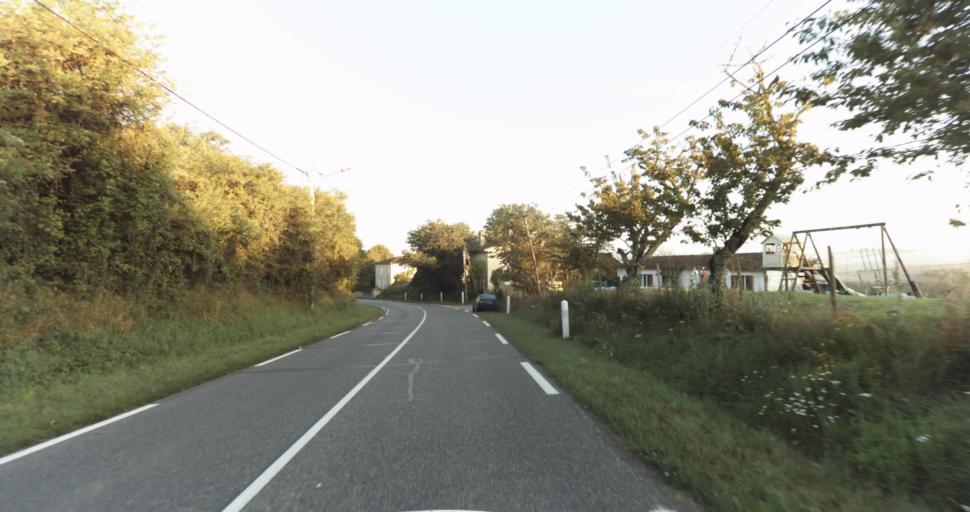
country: FR
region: Aquitaine
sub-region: Departement de la Gironde
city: Bazas
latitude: 44.4308
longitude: -0.1976
